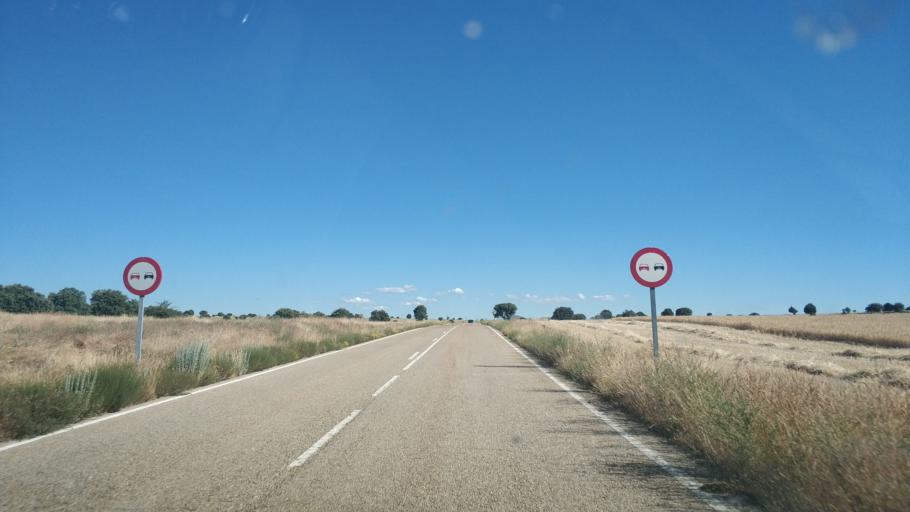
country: ES
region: Castille and Leon
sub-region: Provincia de Soria
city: Montejo de Tiermes
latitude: 41.3943
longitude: -3.1984
